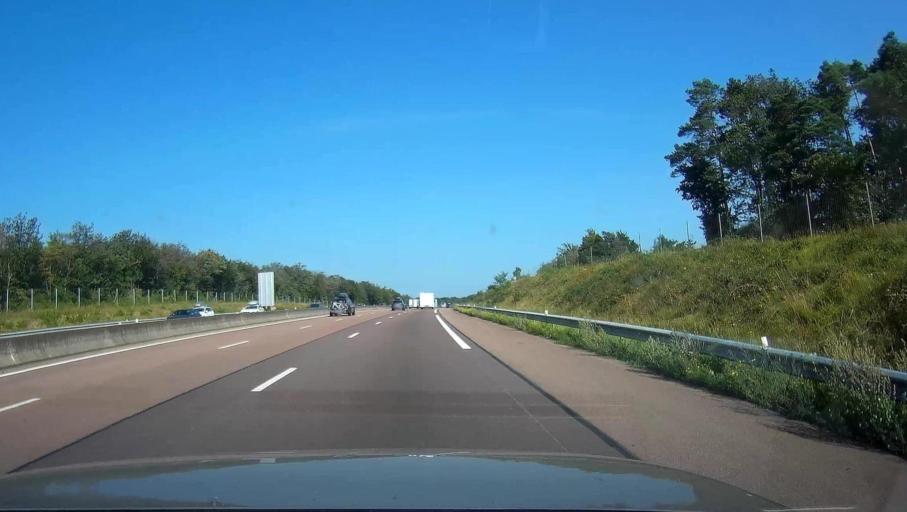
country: FR
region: Bourgogne
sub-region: Departement de la Cote-d'Or
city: Selongey
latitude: 47.6153
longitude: 5.1826
